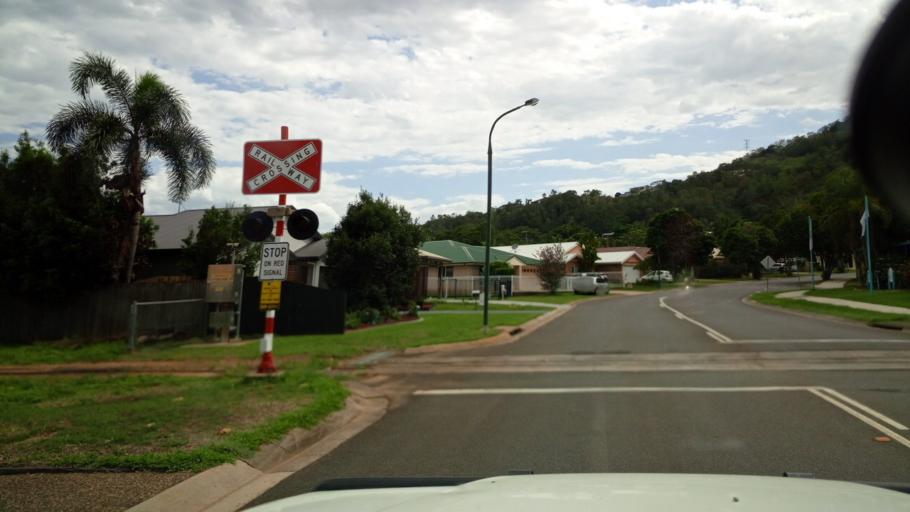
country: AU
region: Queensland
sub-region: Cairns
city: Woree
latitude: -16.9260
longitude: 145.7270
